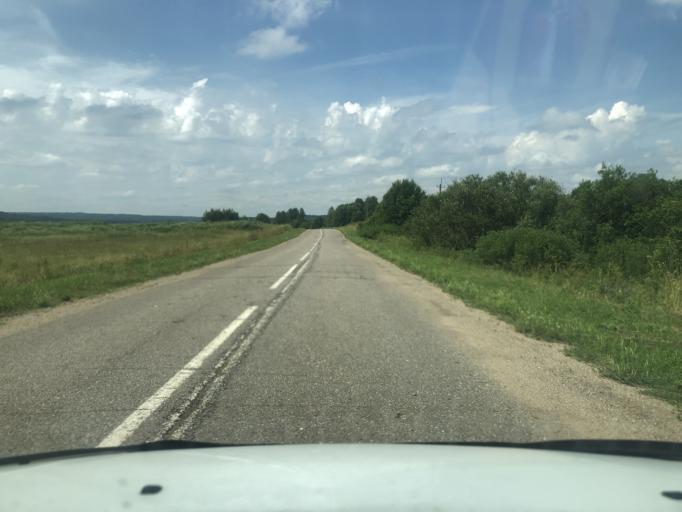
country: RU
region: Jaroslavl
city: Pereslavl'-Zalesskiy
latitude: 57.0399
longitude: 38.8810
